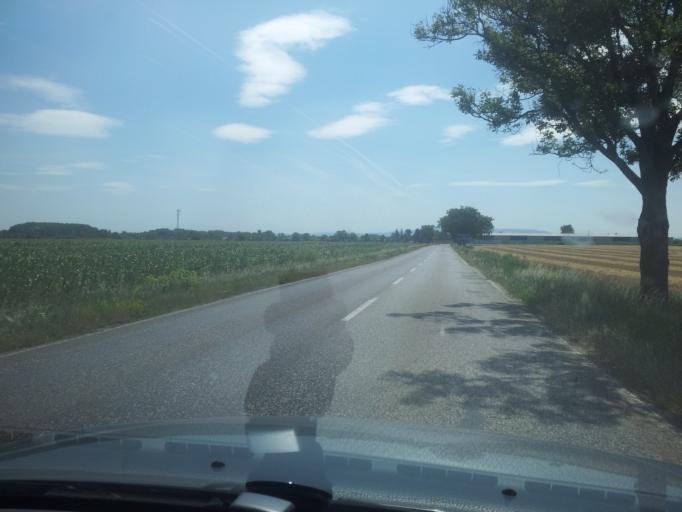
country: SK
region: Nitriansky
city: Zeliezovce
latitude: 48.1157
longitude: 18.6189
